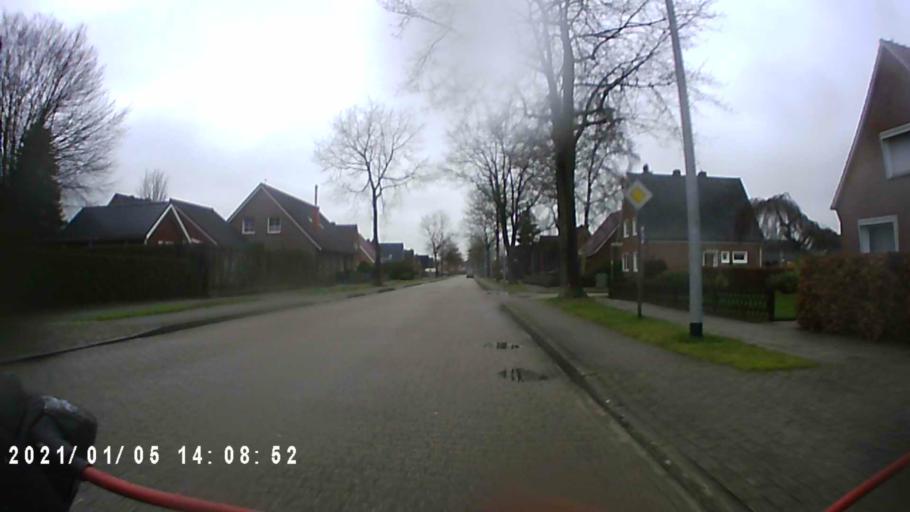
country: DE
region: Lower Saxony
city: Weener
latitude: 53.1657
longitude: 7.3400
